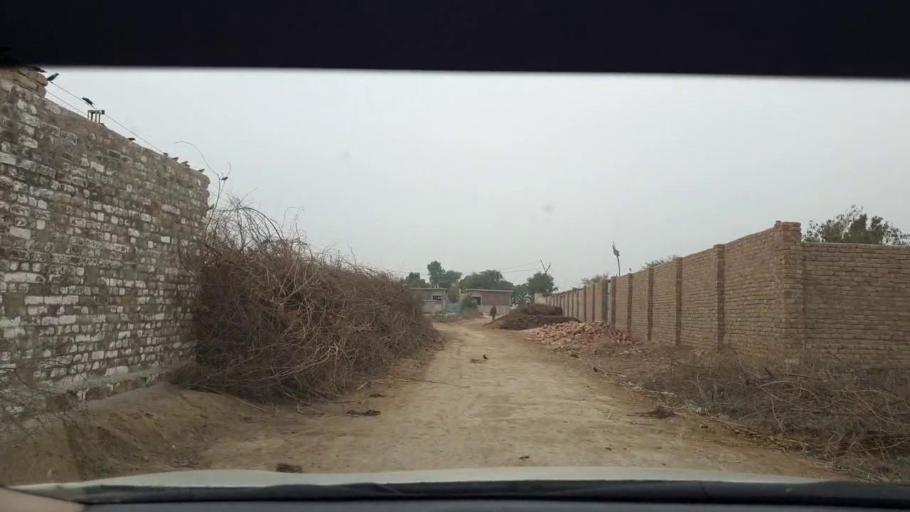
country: PK
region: Sindh
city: Berani
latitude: 25.8564
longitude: 68.7919
